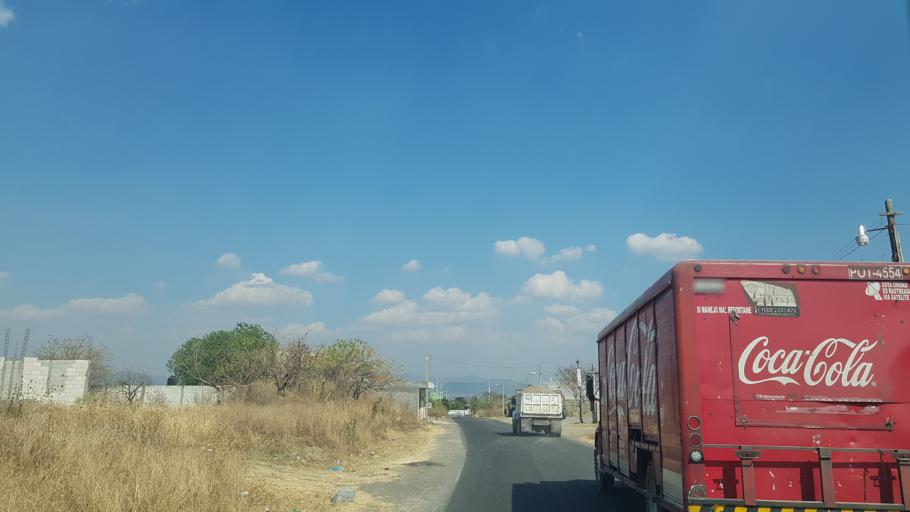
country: MX
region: Puebla
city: Atlixco
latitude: 18.9114
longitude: -98.4770
